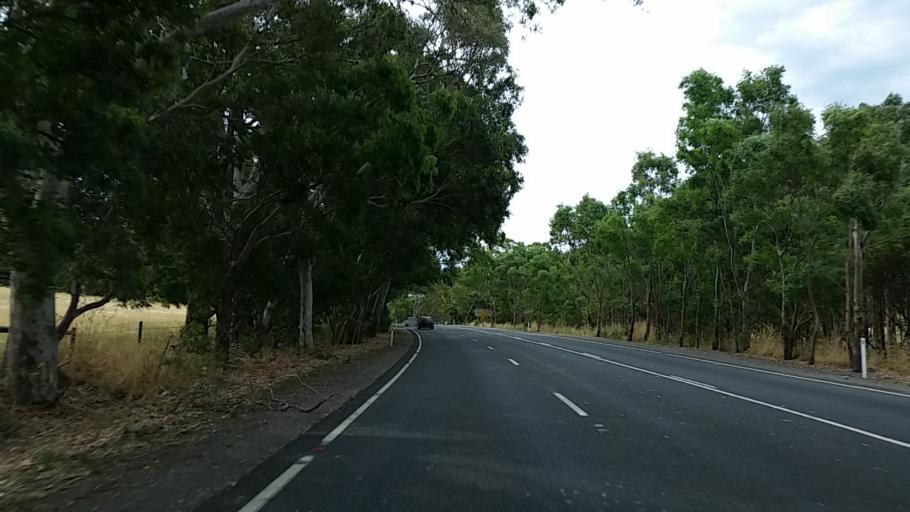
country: AU
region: South Australia
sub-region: Onkaparinga
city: Aldinga
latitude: -35.3730
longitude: 138.4628
